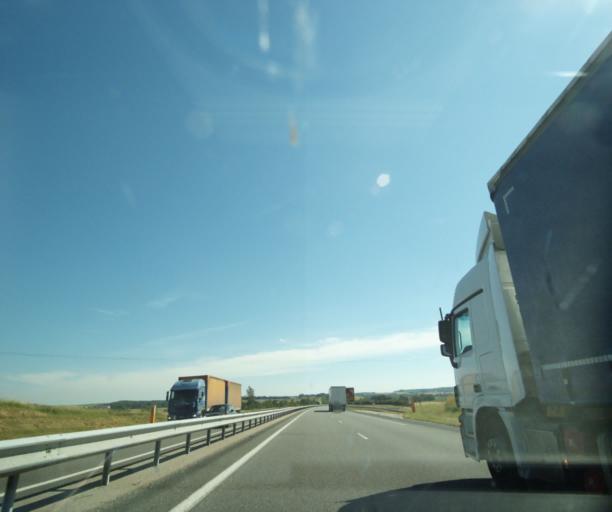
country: FR
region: Lorraine
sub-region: Departement des Vosges
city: Bulgneville
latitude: 48.2013
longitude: 5.7931
